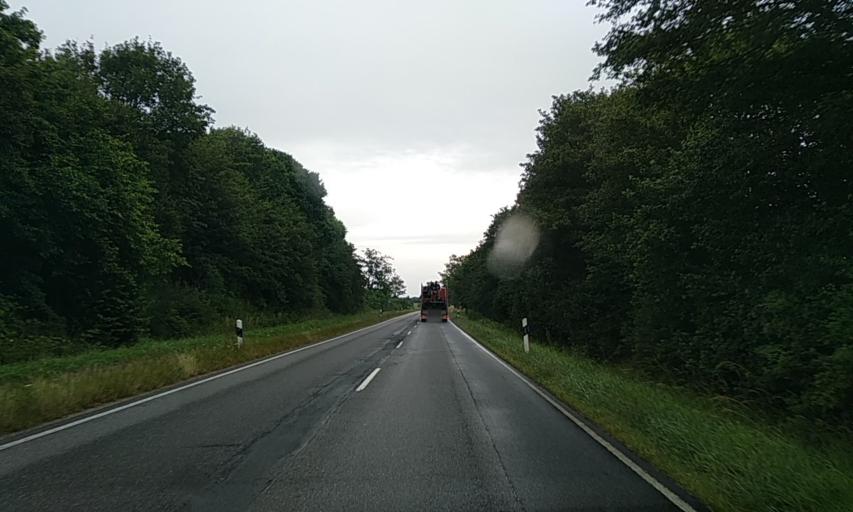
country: DE
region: Schleswig-Holstein
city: Loit
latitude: 54.6384
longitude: 9.6881
